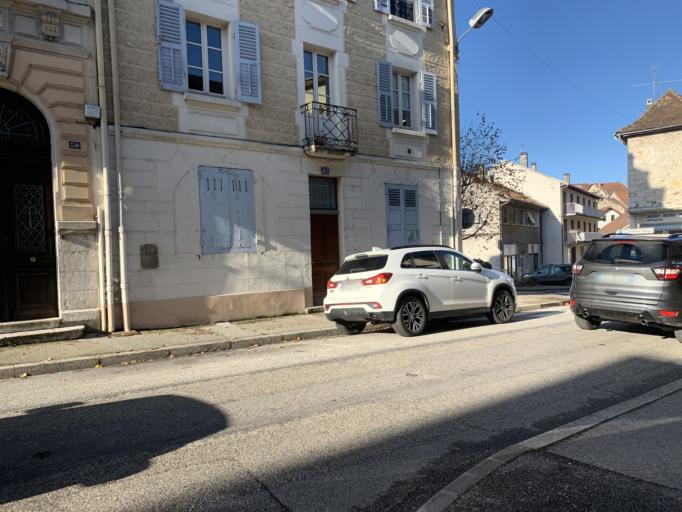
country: FR
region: Rhone-Alpes
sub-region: Departement de l'Ain
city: Belley
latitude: 45.7583
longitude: 5.6864
